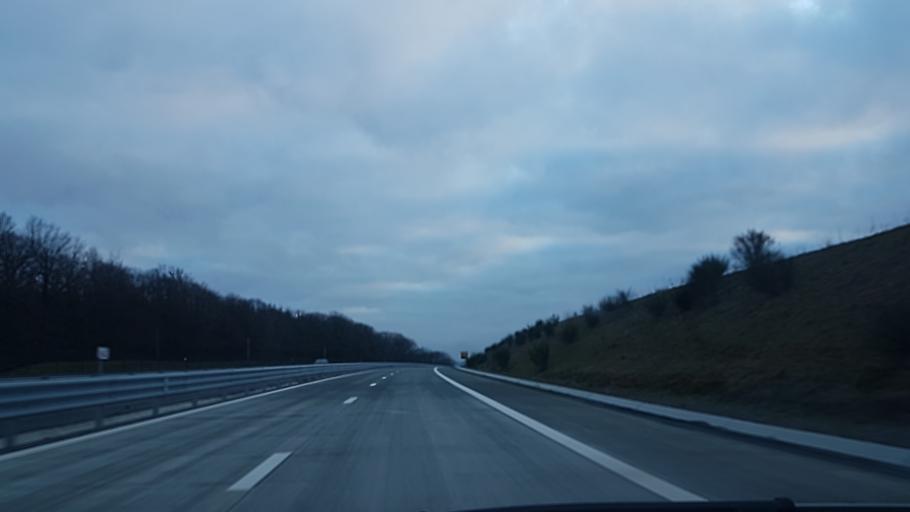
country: FR
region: Champagne-Ardenne
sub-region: Departement des Ardennes
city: Rocroi
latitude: 49.9945
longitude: 4.5430
